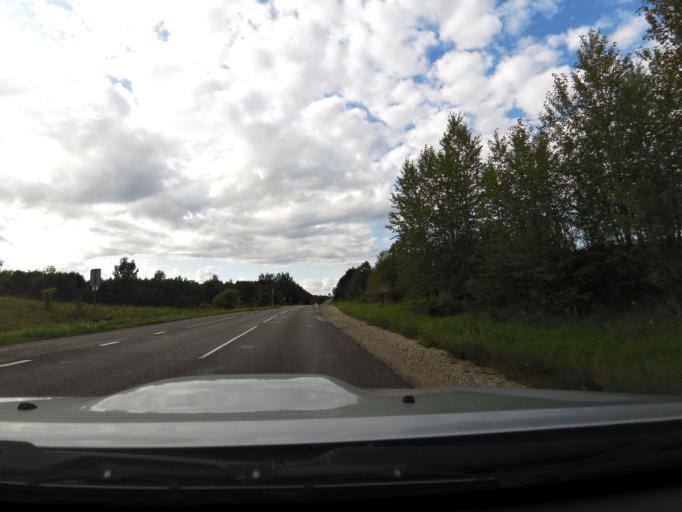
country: LV
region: Akniste
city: Akniste
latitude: 56.0147
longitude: 25.9269
